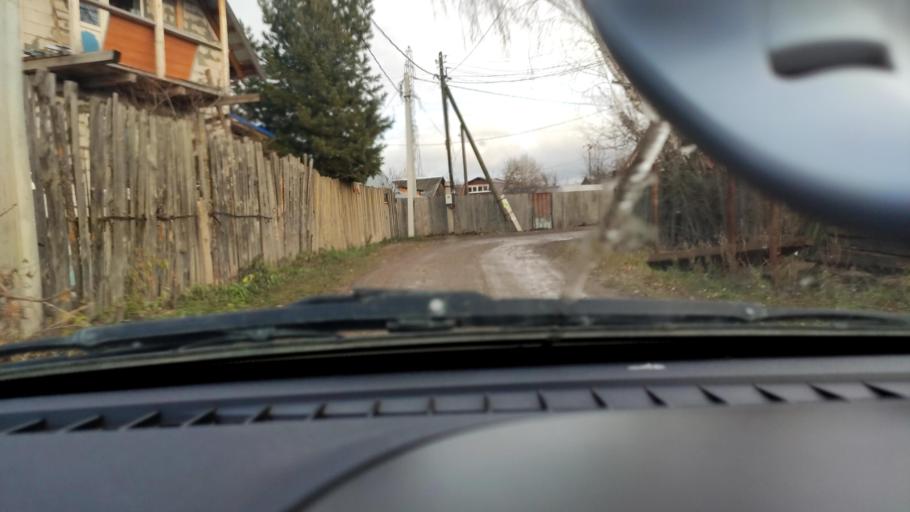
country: RU
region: Perm
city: Kondratovo
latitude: 57.9569
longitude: 56.1450
